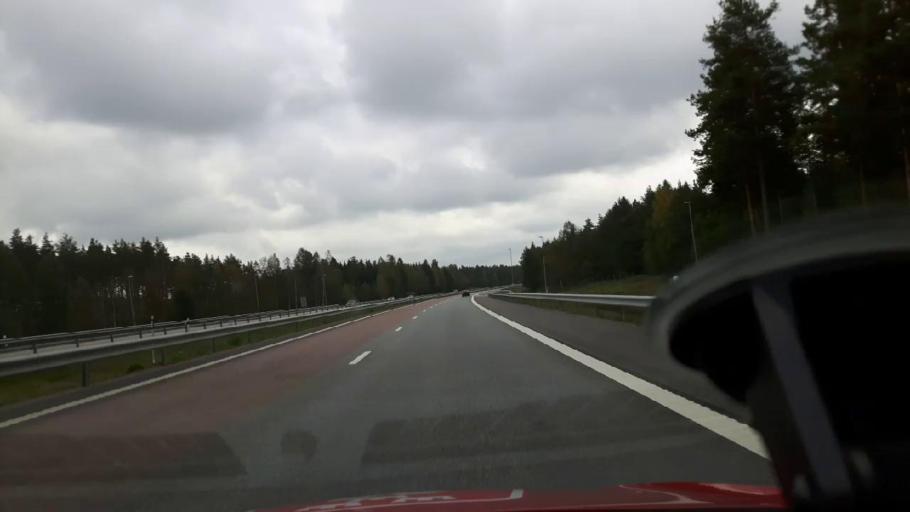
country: SE
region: Gaevleborg
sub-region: Gavle Kommun
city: Gavle
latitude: 60.6386
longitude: 17.1401
